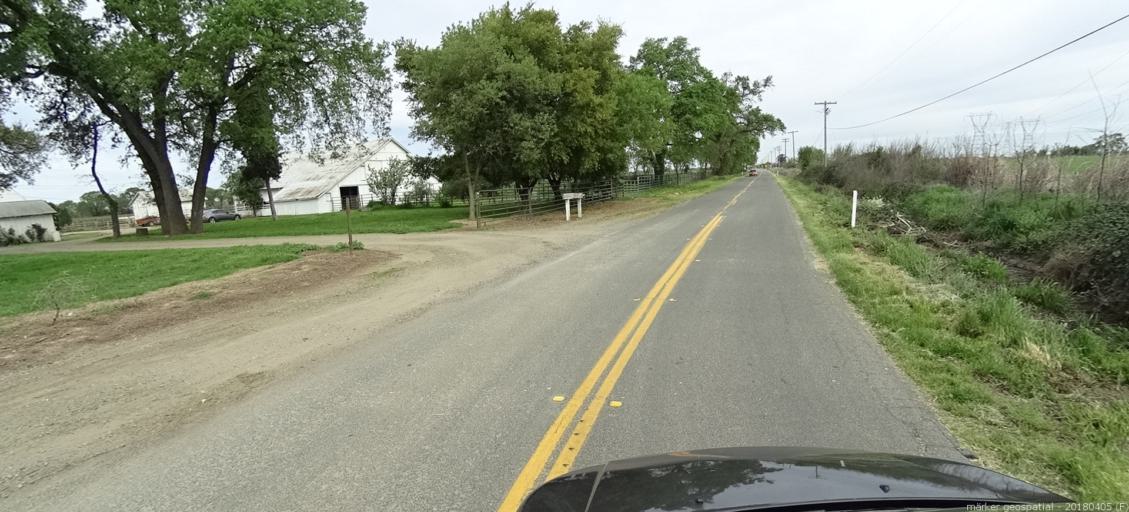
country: US
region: California
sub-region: San Joaquin County
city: Thornton
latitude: 38.2402
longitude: -121.3691
